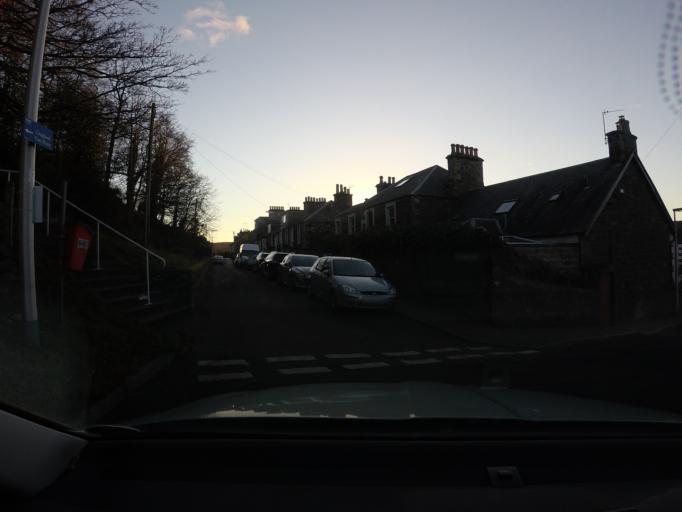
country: GB
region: Scotland
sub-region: Fife
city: Newport-On-Tay
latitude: 56.4431
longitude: -2.9367
